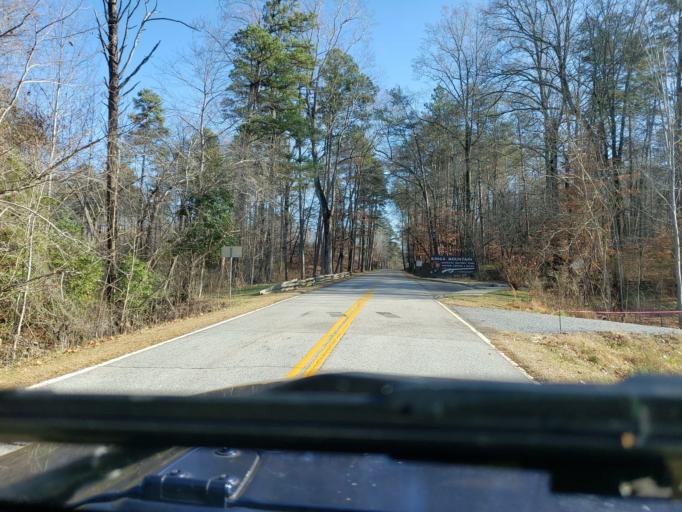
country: US
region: North Carolina
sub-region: Cleveland County
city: White Plains
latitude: 35.1530
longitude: -81.3958
